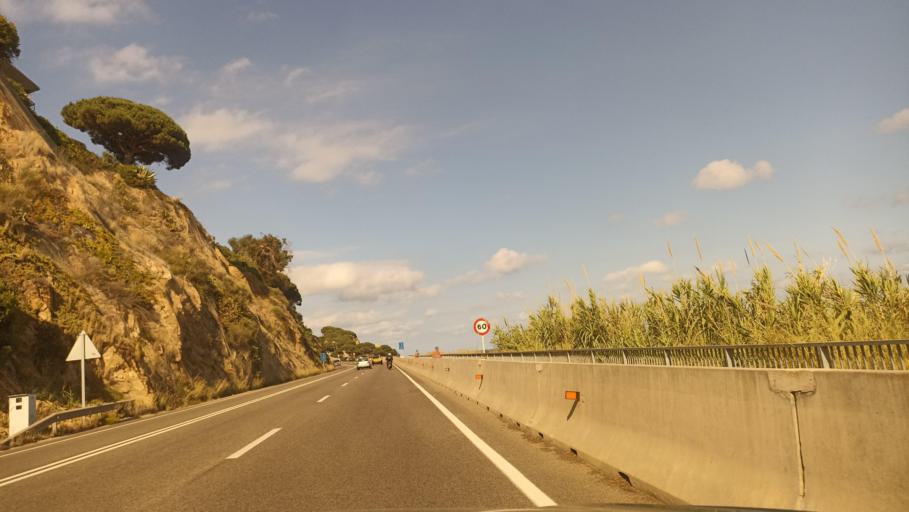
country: ES
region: Catalonia
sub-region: Provincia de Barcelona
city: Sant Pol de Mar
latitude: 41.6044
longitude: 2.6328
